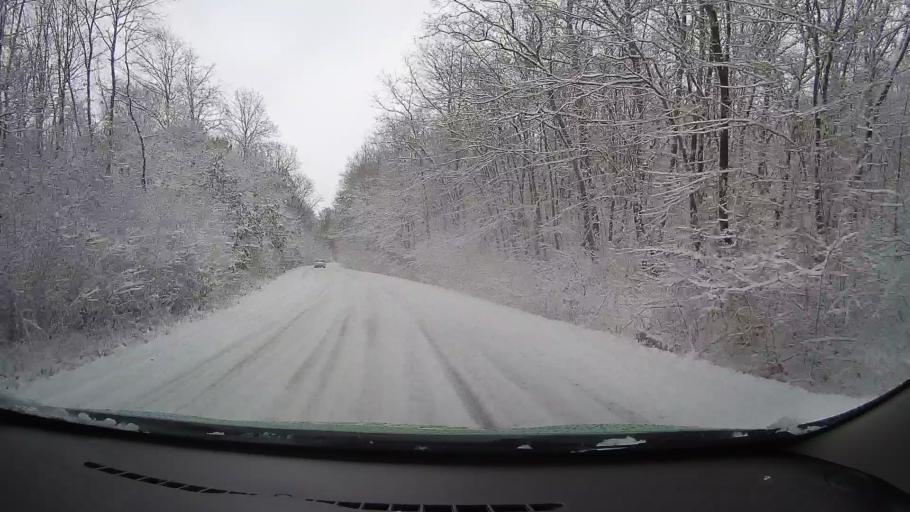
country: RO
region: Hunedoara
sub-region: Municipiul Hunedoara
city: Pestisu Mare
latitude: 45.8103
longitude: 22.9052
